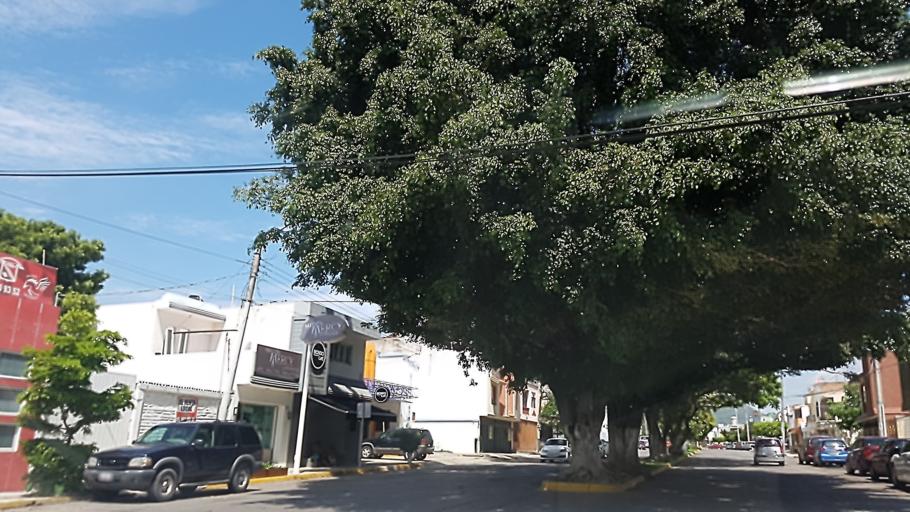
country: MX
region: Nayarit
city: Tepic
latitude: 21.4856
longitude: -104.8835
